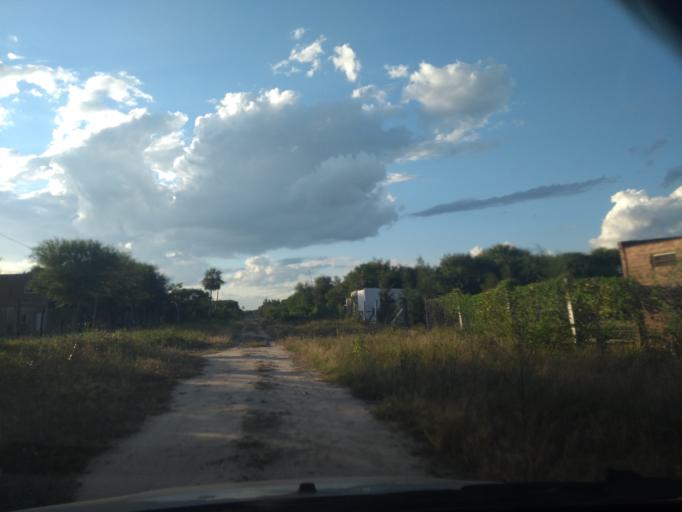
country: AR
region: Chaco
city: Colonia Benitez
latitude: -27.3899
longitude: -58.9442
